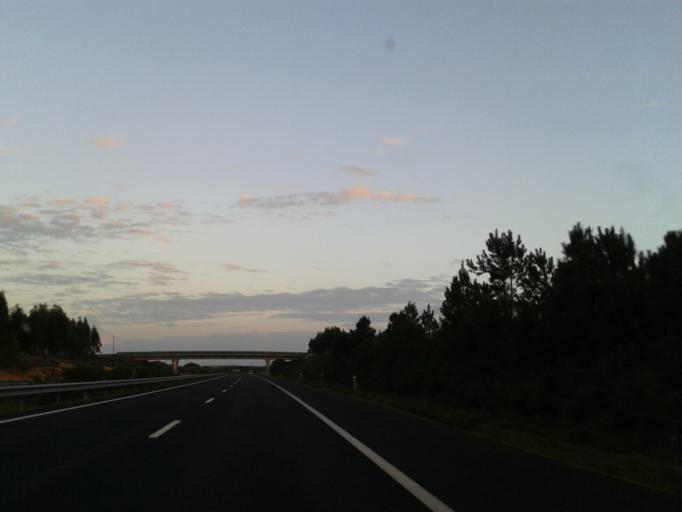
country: PT
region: Santarem
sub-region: Benavente
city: Poceirao
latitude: 38.7192
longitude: -8.6602
